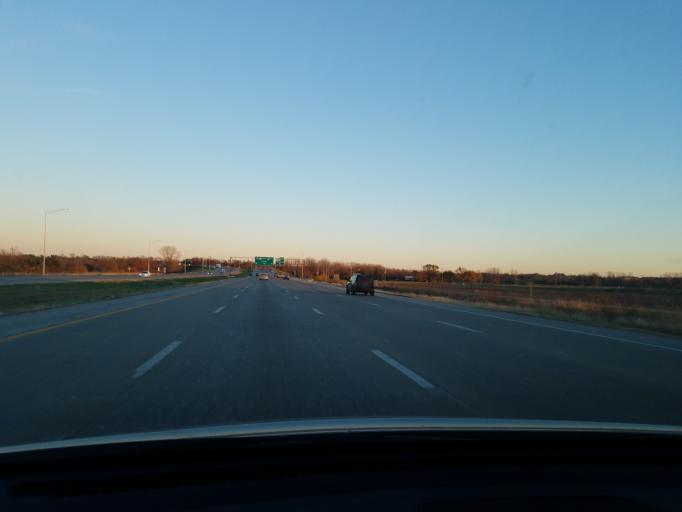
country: US
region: Illinois
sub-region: Saint Clair County
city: Dupo
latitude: 38.4764
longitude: -90.2417
